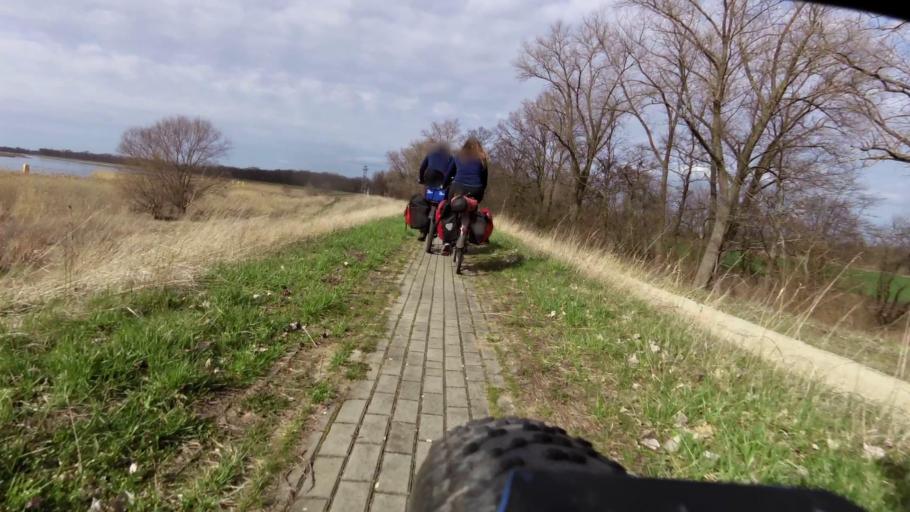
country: PL
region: Lubusz
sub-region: Powiat slubicki
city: Gorzyca
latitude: 52.4979
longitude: 14.6377
